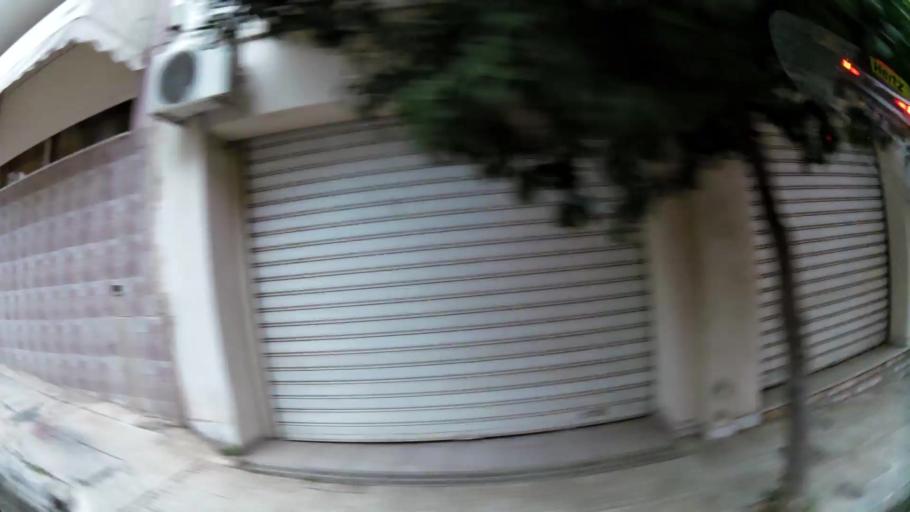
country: GR
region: Attica
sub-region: Nomarchia Athinas
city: Agia Varvara
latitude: 37.9944
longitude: 23.6581
